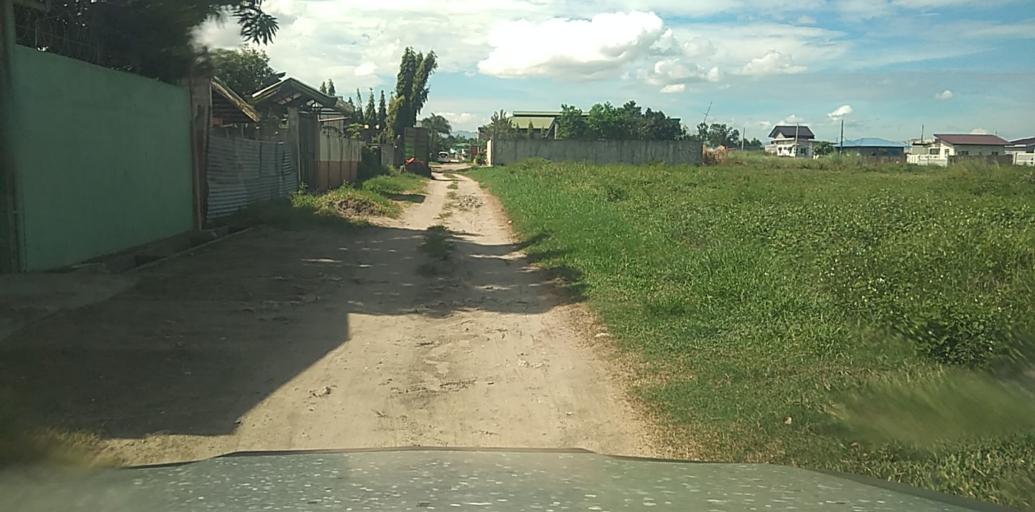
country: PH
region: Central Luzon
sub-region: Province of Pampanga
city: Buensuseso
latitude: 15.1940
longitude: 120.6692
